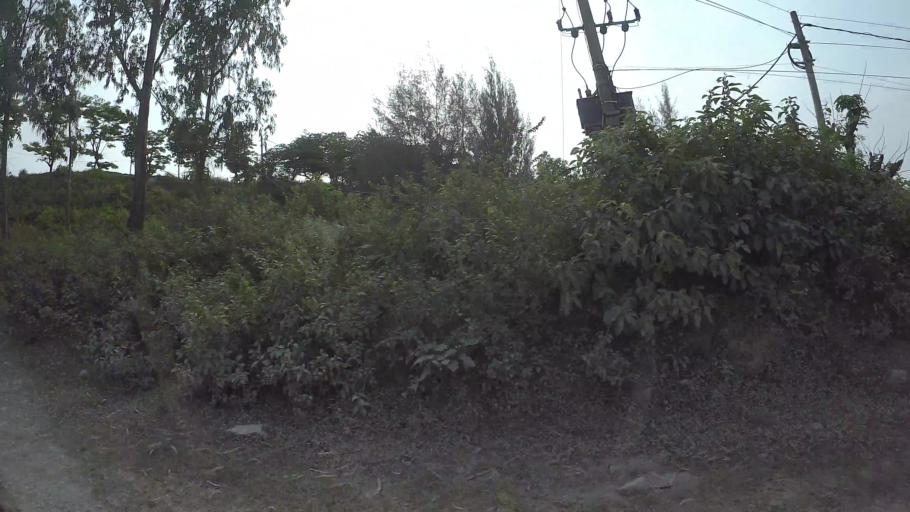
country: VN
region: Da Nang
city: Lien Chieu
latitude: 16.0417
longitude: 108.1496
